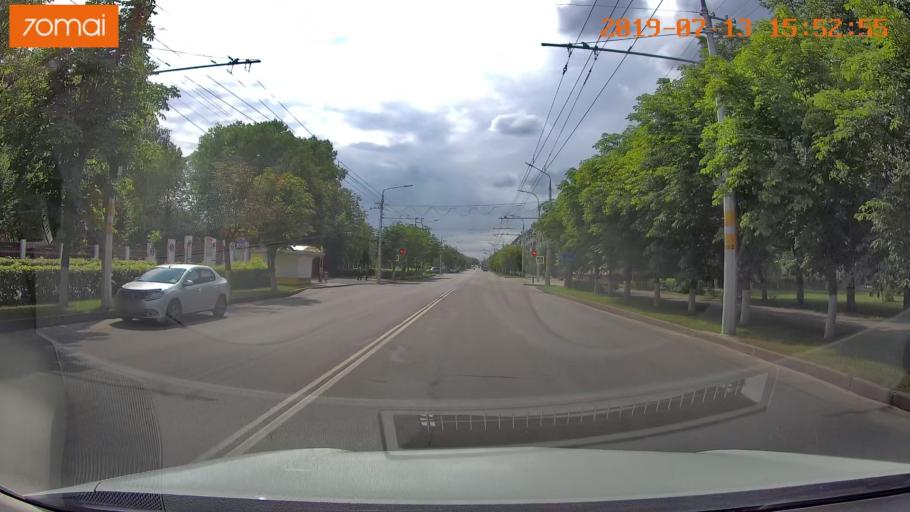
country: BY
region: Mogilev
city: Babruysk
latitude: 53.1389
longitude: 29.2097
